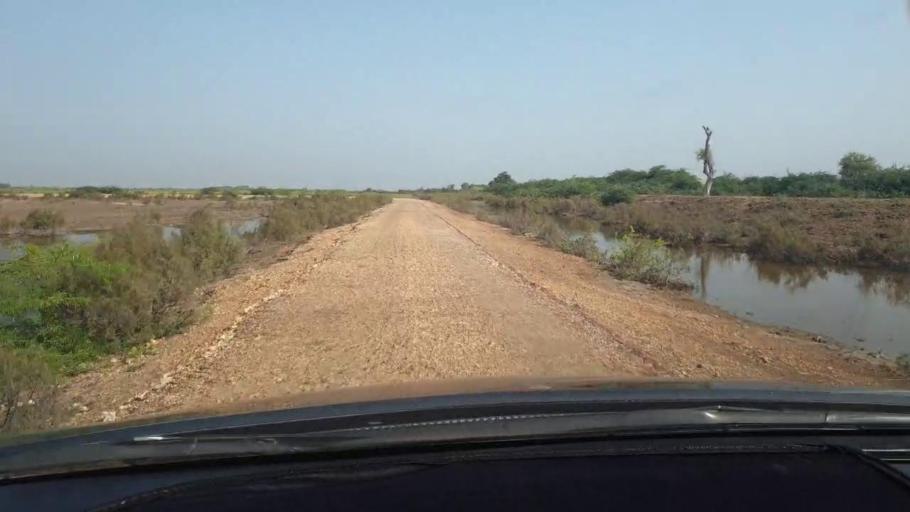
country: PK
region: Sindh
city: Tando Bago
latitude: 24.6784
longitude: 69.1688
